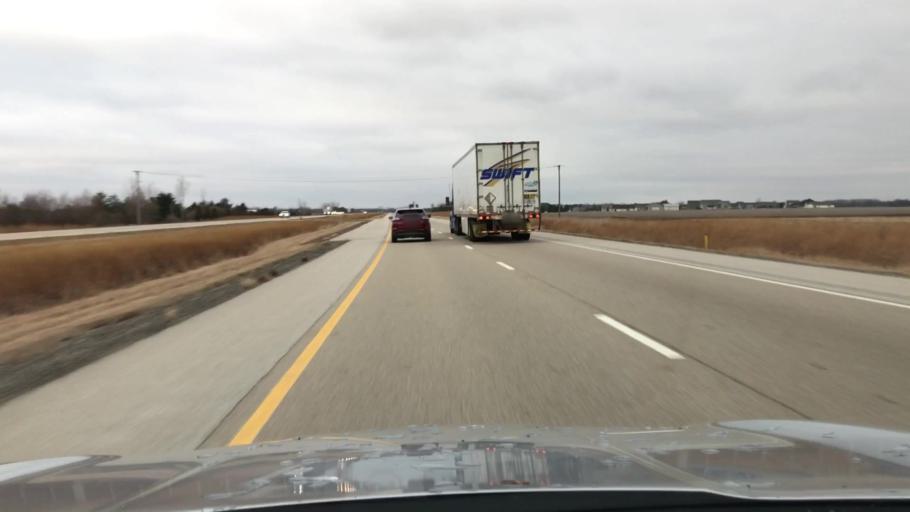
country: US
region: Illinois
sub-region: Logan County
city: Lincoln
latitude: 40.1849
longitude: -89.3282
